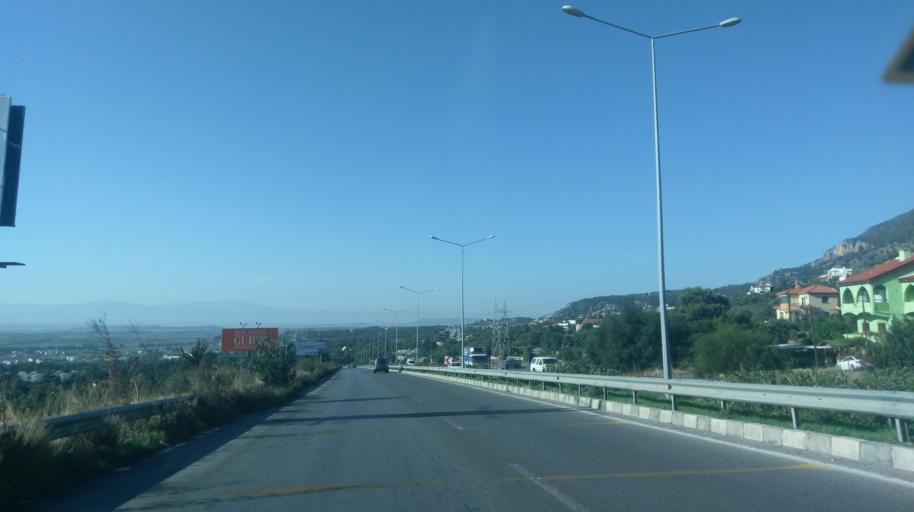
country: CY
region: Keryneia
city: Kyrenia
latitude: 35.2994
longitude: 33.2834
